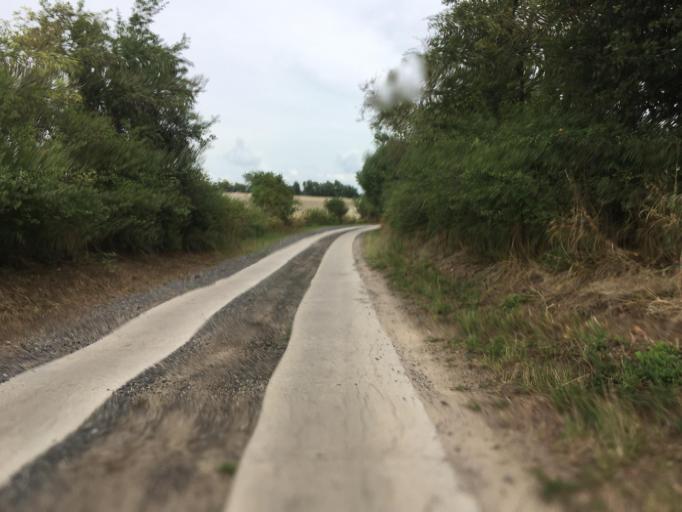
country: DE
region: Brandenburg
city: Gerswalde
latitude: 53.2032
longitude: 13.8310
